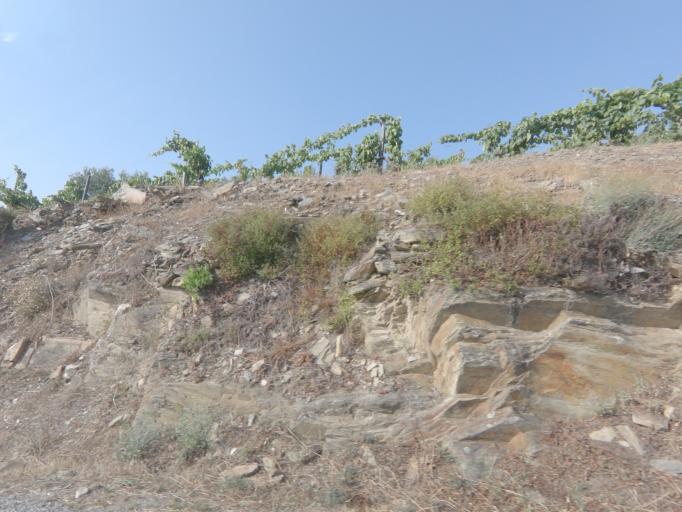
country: PT
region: Viseu
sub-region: Tabuaco
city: Tabuaco
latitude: 41.1598
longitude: -7.5615
